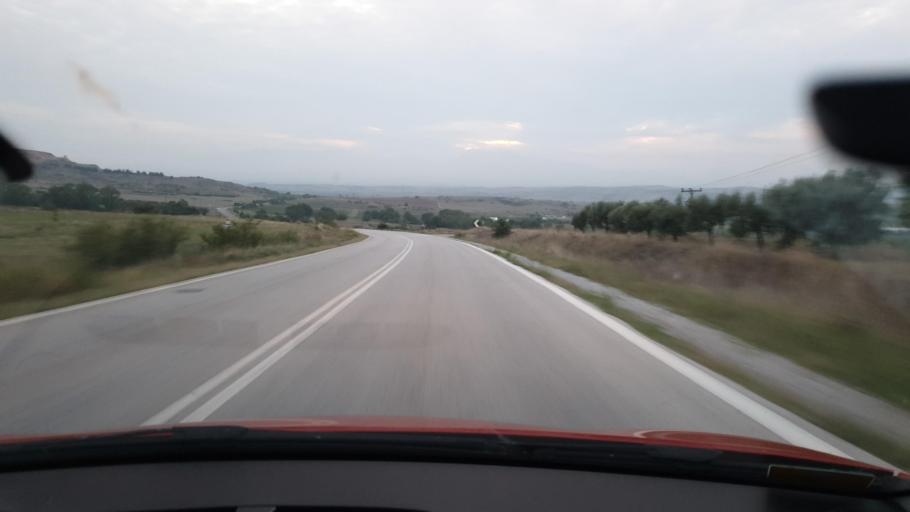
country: GR
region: Central Macedonia
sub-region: Nomos Kilkis
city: Polykastro
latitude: 41.0181
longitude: 22.6633
